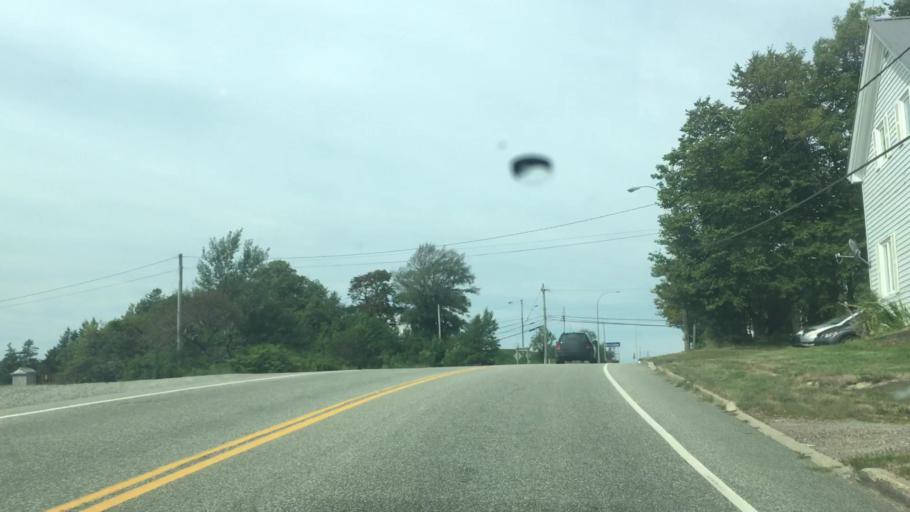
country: CA
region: Nova Scotia
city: Port Hawkesbury
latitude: 45.6448
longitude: -61.3995
